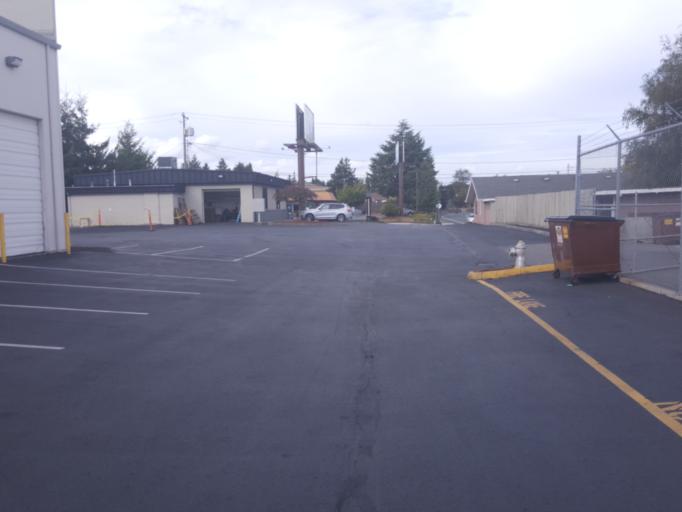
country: US
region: Washington
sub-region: Pierce County
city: Fircrest
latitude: 47.2346
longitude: -122.5304
